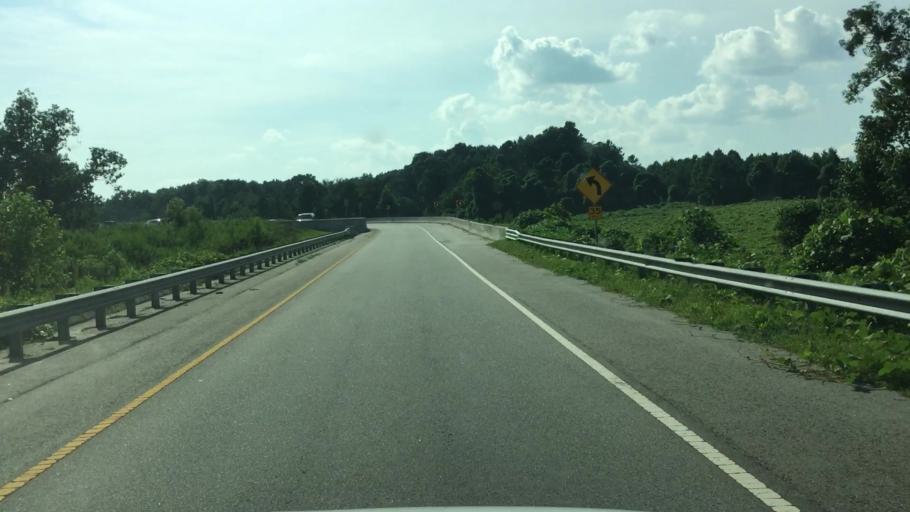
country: US
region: Georgia
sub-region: Gwinnett County
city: Dacula
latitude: 33.9751
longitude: -83.9057
